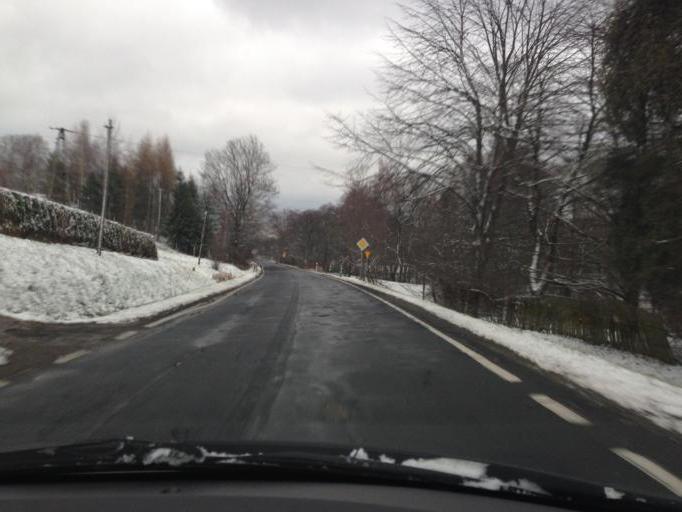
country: PL
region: Lesser Poland Voivodeship
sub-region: Powiat brzeski
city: Iwkowa
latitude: 49.8508
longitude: 20.6033
